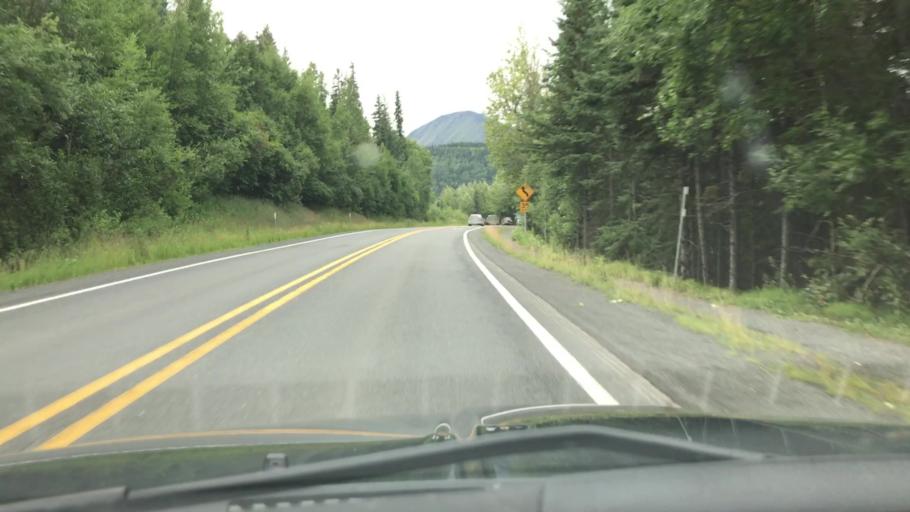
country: US
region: Alaska
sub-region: Kenai Peninsula Borough
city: Seward
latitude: 60.4863
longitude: -149.8687
